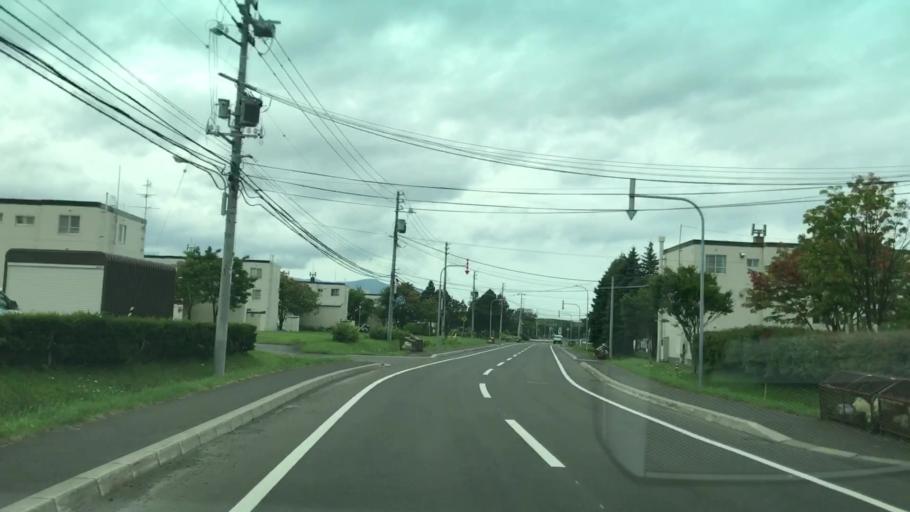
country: JP
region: Hokkaido
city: Iwanai
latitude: 43.0340
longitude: 140.5392
